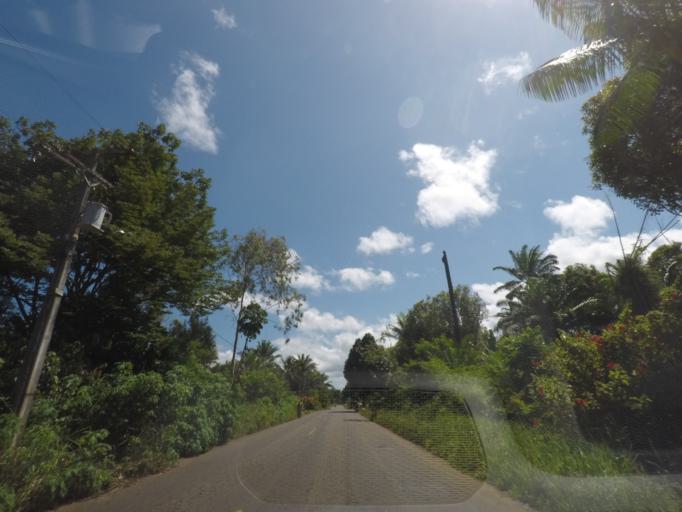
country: BR
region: Bahia
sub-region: Taperoa
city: Taperoa
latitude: -13.4889
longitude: -39.0923
